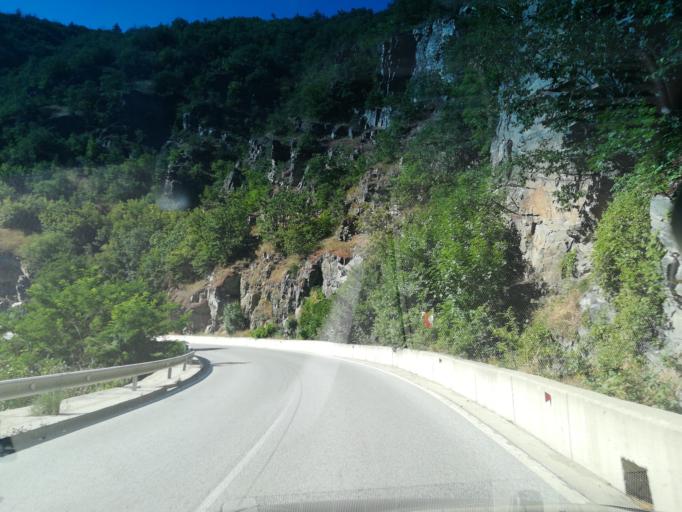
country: BG
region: Plovdiv
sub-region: Obshtina Luki
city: Luki
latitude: 41.9062
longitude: 24.7636
